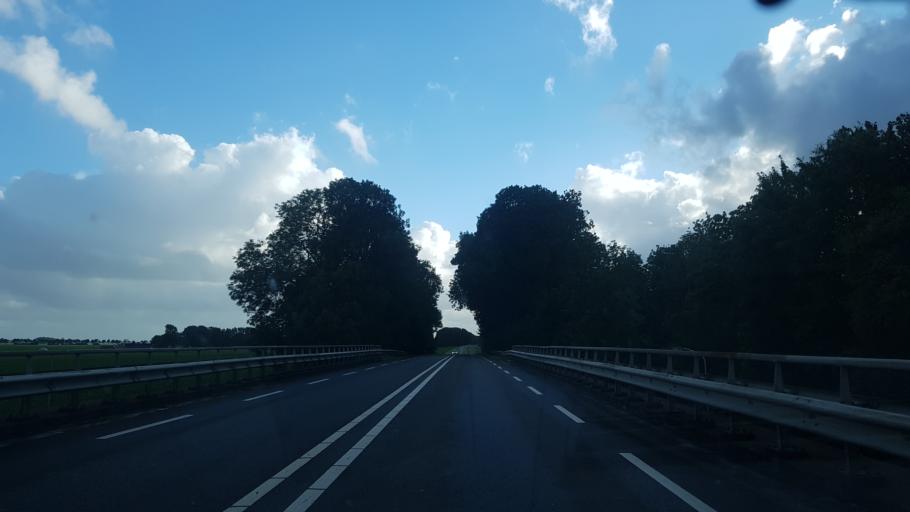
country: NL
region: Groningen
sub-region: Gemeente Slochteren
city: Slochteren
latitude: 53.3100
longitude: 6.7499
